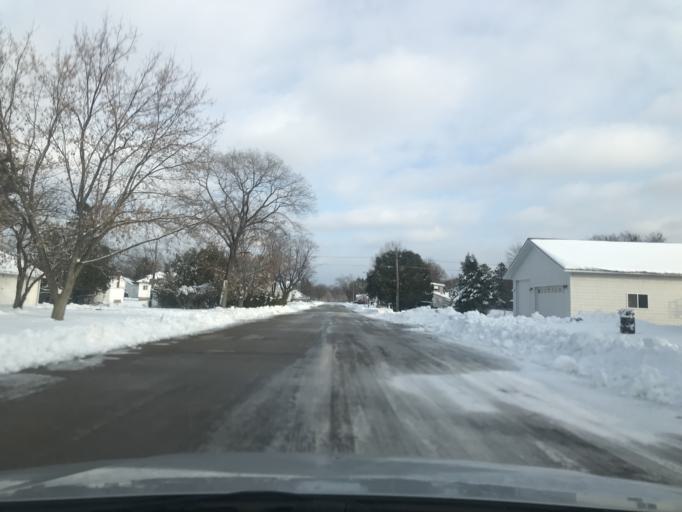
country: US
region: Wisconsin
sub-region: Marinette County
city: Peshtigo
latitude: 45.0485
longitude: -87.7526
